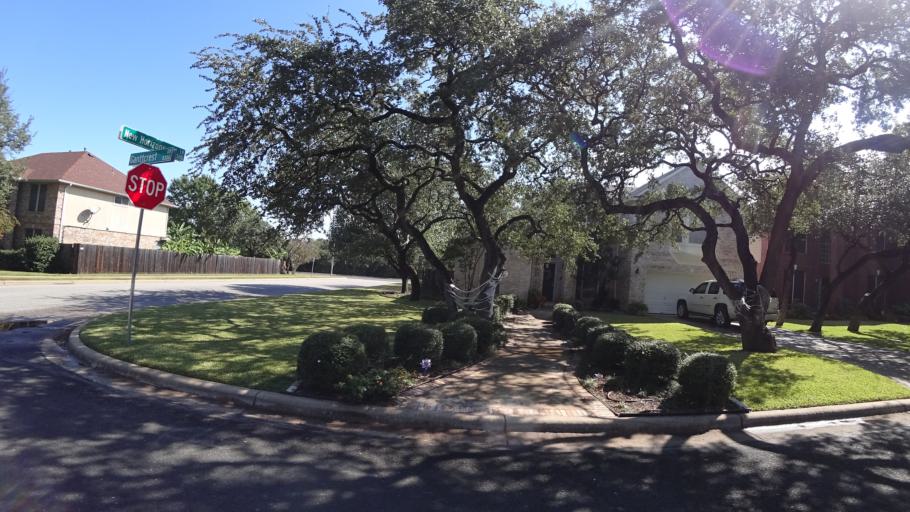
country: US
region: Texas
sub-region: Travis County
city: Shady Hollow
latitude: 30.2127
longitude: -97.8655
